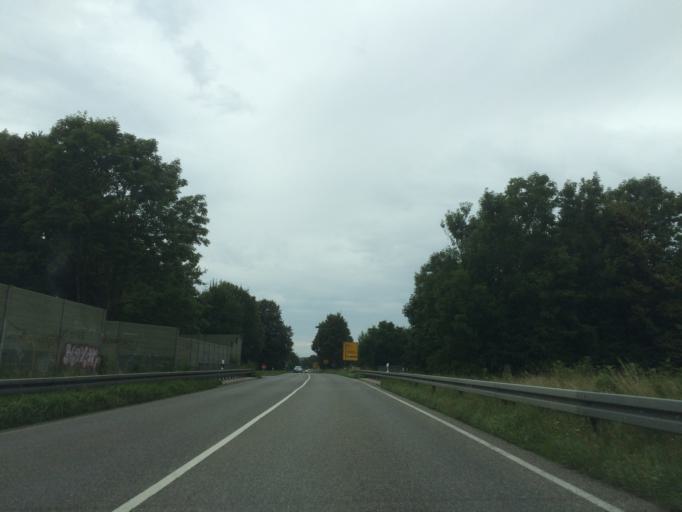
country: DE
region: Baden-Wuerttemberg
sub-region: Tuebingen Region
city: Bad Waldsee
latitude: 47.9303
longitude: 9.7660
